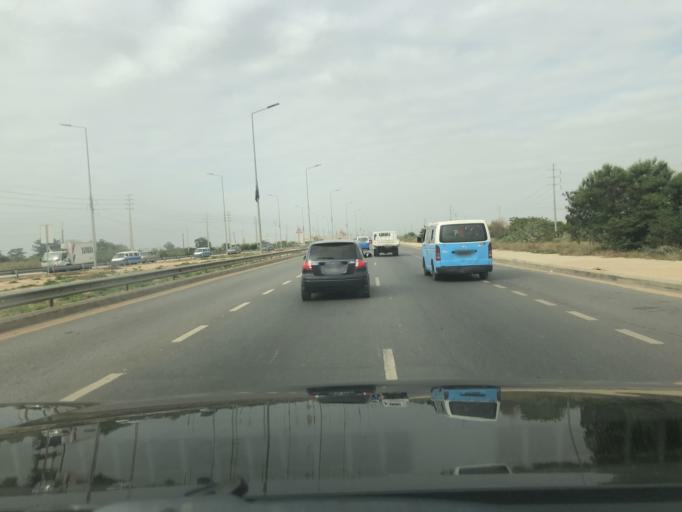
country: AO
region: Luanda
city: Luanda
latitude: -8.9476
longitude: 13.2597
